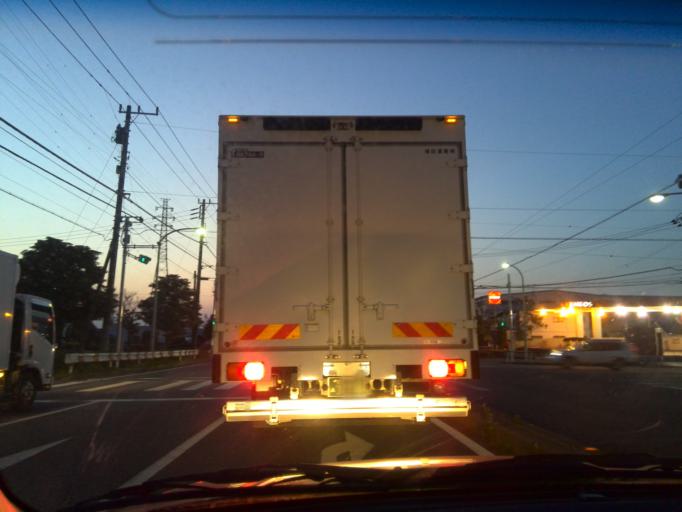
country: JP
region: Chiba
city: Funabashi
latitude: 35.6670
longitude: 140.0061
